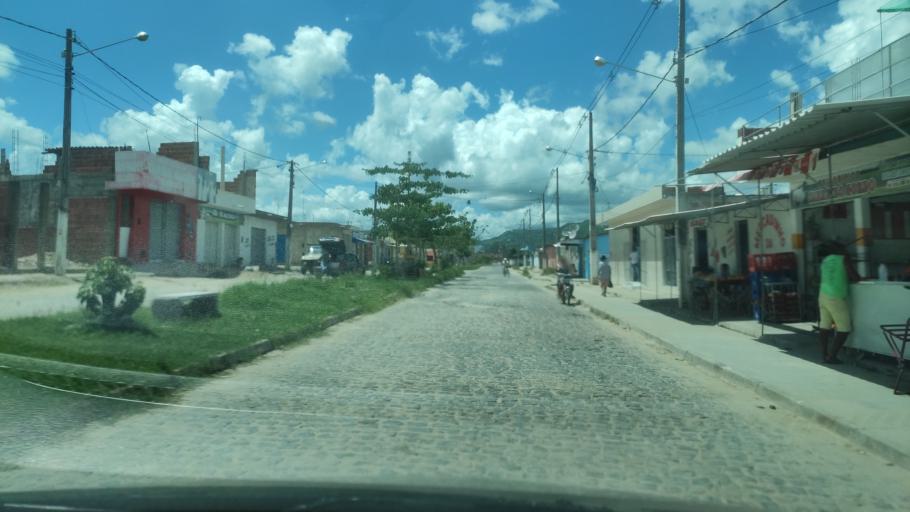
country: BR
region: Alagoas
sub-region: Uniao Dos Palmares
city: Uniao dos Palmares
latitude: -9.1487
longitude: -36.0057
